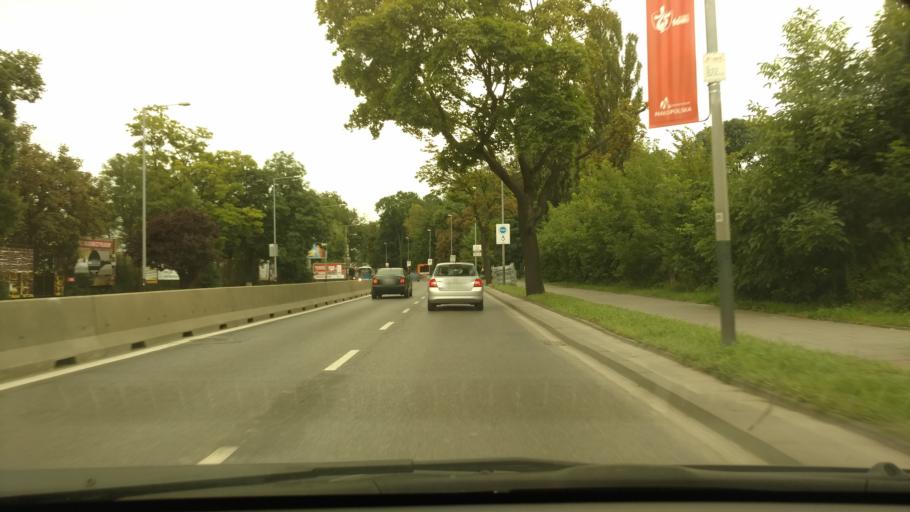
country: PL
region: Lesser Poland Voivodeship
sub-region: Krakow
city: Krakow
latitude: 50.0400
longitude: 19.9368
